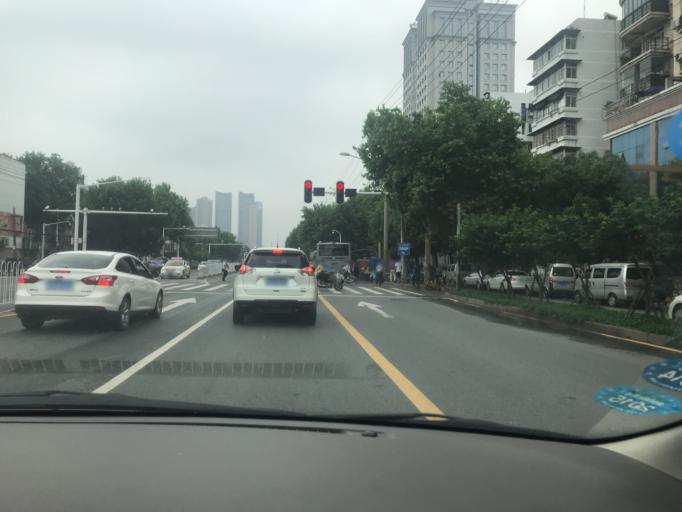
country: CN
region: Hubei
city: Jiang'an
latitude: 30.6063
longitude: 114.3419
